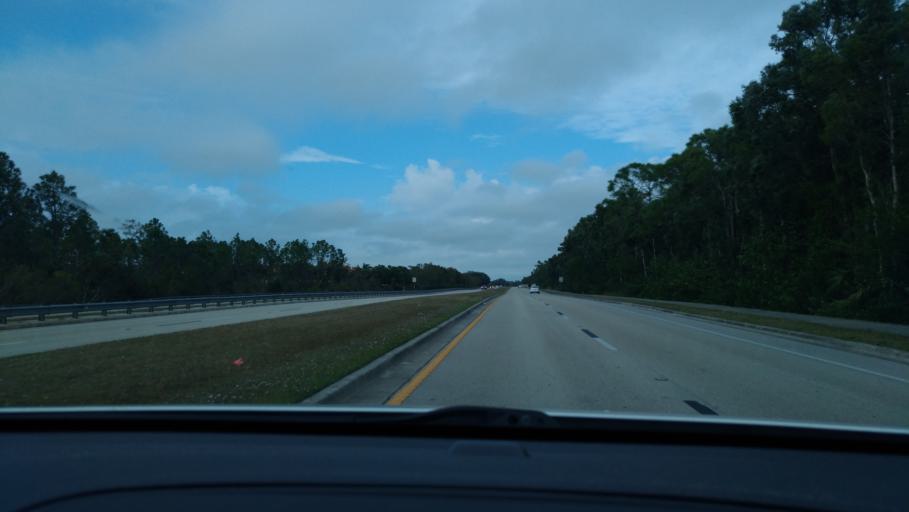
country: US
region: Florida
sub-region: Lee County
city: Estero
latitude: 26.4086
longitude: -81.8046
